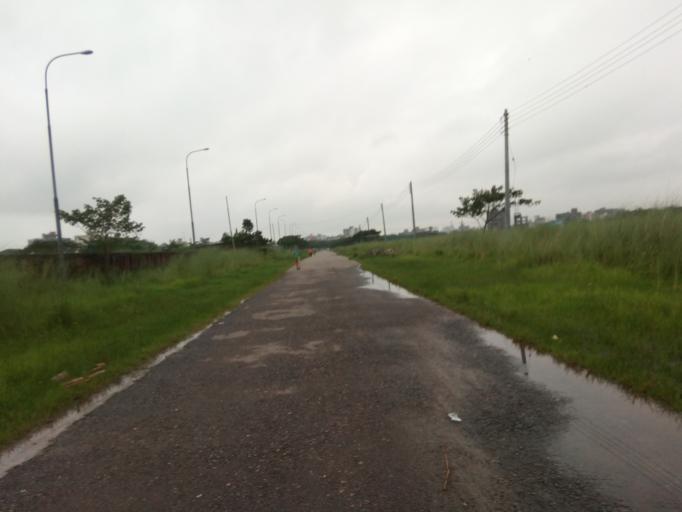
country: BD
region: Dhaka
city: Tungi
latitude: 23.8476
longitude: 90.4307
